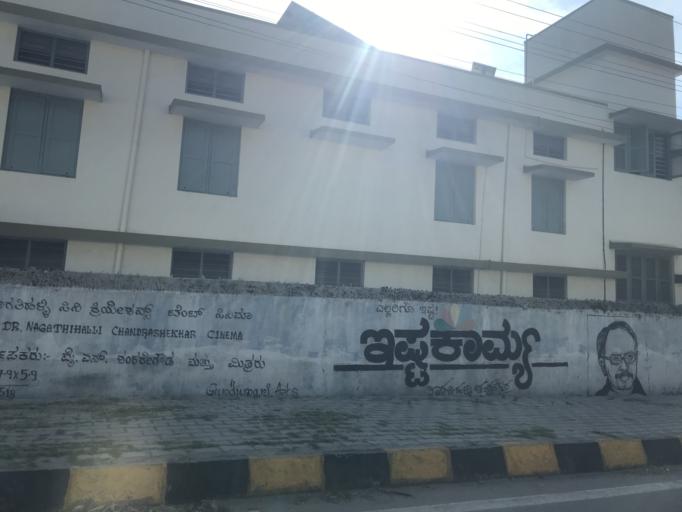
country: IN
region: Karnataka
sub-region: Mysore
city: Mysore
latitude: 12.2849
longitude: 76.6407
